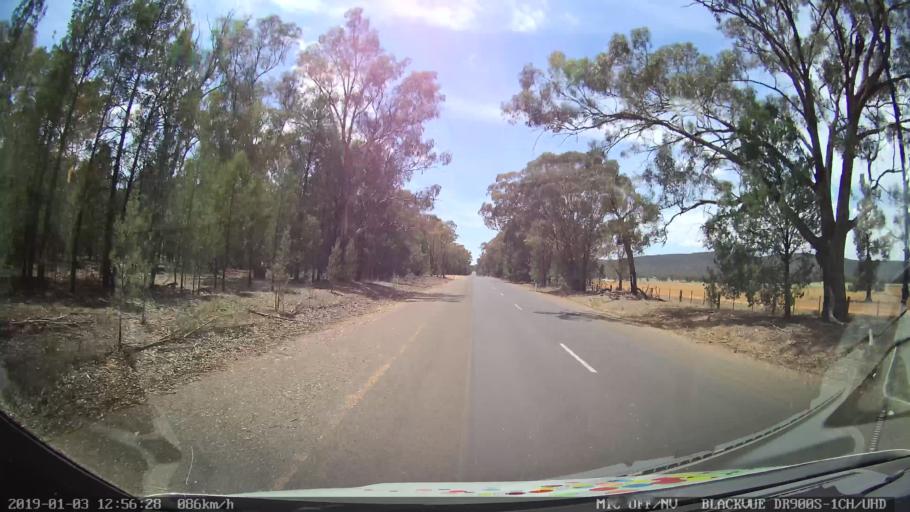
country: AU
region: New South Wales
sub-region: Weddin
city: Grenfell
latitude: -33.6462
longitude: 148.3460
